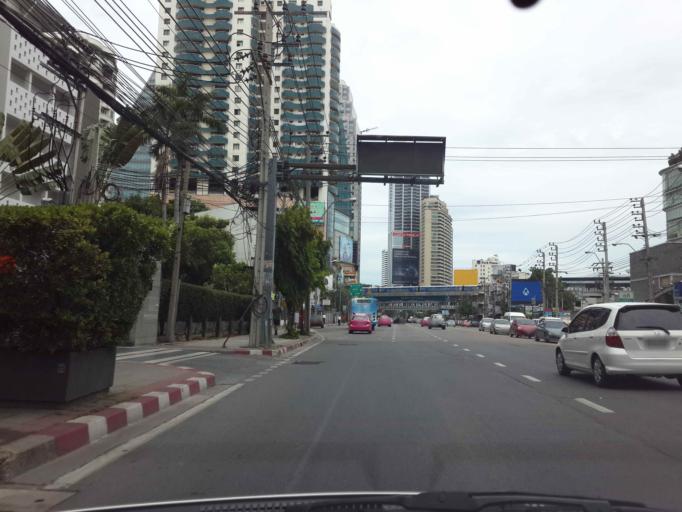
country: TH
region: Bangkok
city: Khlong Toei
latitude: 13.7392
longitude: 100.5617
